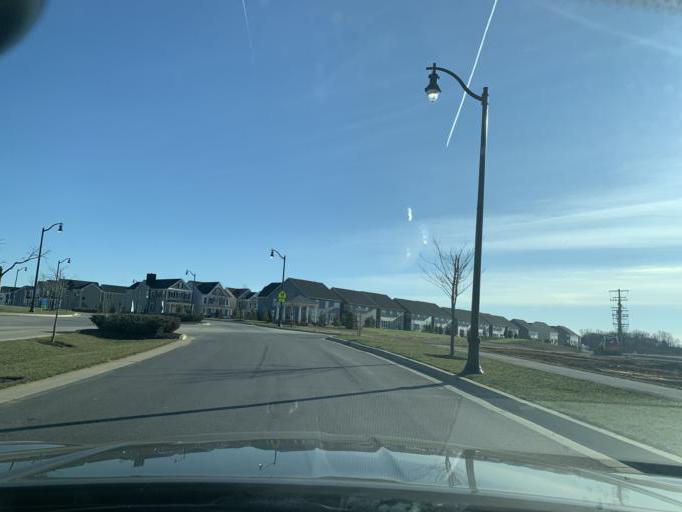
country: US
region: Maryland
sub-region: Anne Arundel County
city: Crofton
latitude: 39.0249
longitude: -76.7276
